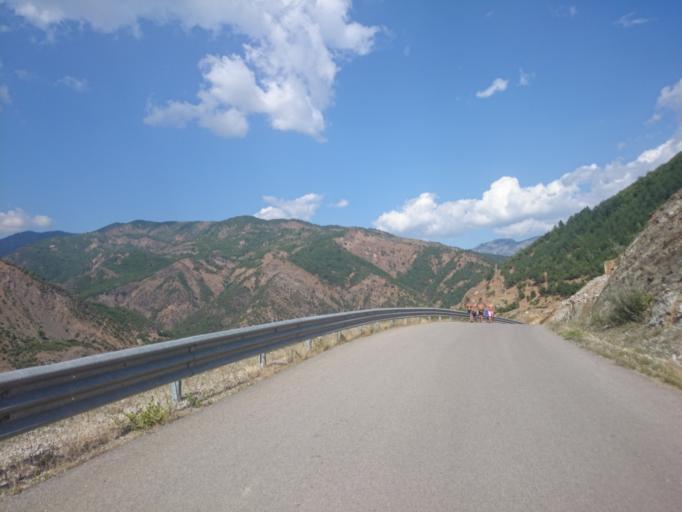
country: AL
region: Lezhe
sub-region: Rrethi i Lezhes
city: Blinisht
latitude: 41.8677
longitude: 20.0251
